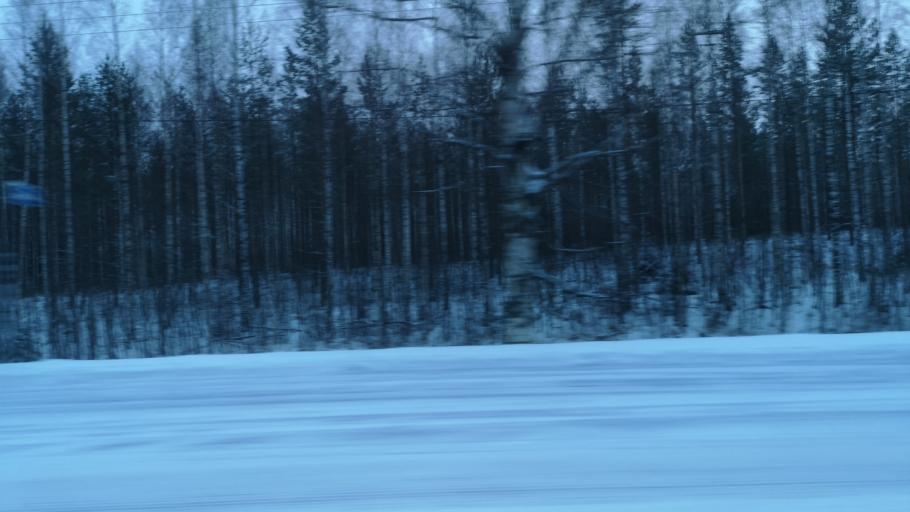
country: FI
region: Southern Savonia
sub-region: Savonlinna
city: Enonkoski
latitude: 62.0965
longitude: 28.6667
